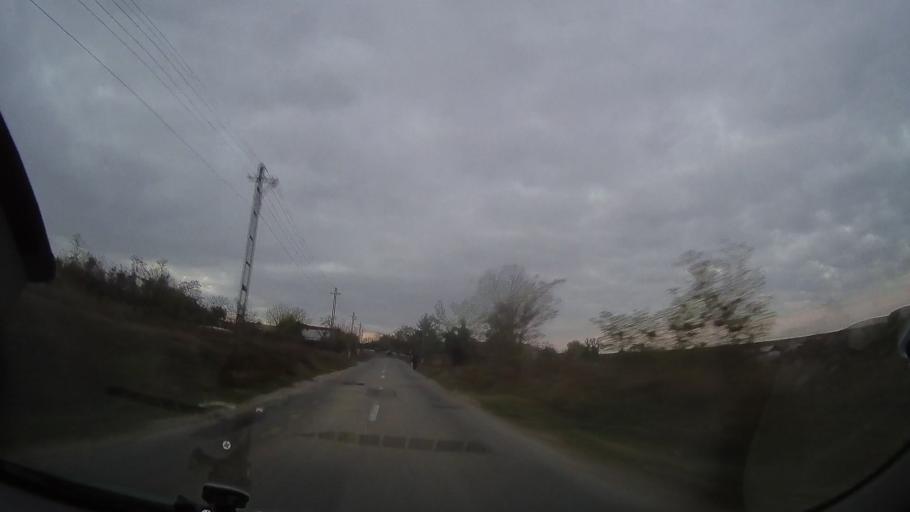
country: RO
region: Tulcea
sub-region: Comuna Mihai Bravu
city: Turda
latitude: 44.9697
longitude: 28.6281
